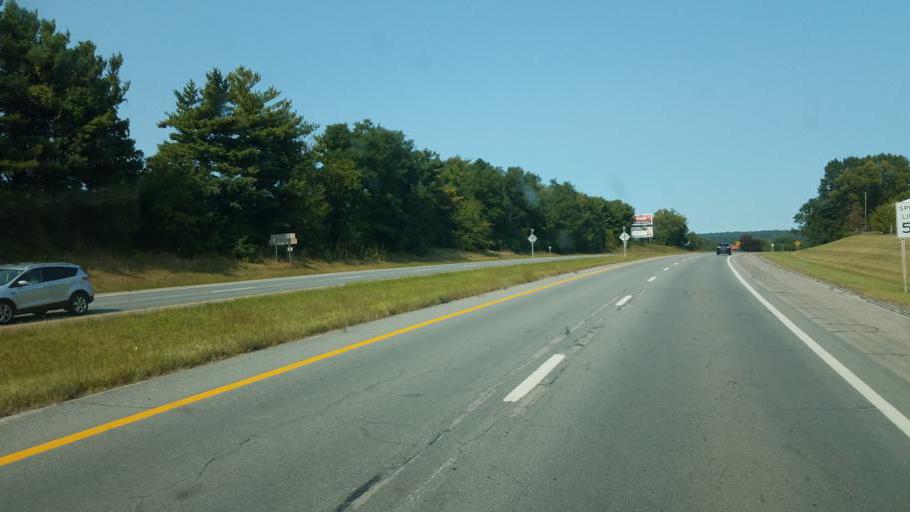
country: US
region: Ohio
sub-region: Wayne County
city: Wooster
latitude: 40.7809
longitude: -81.9678
